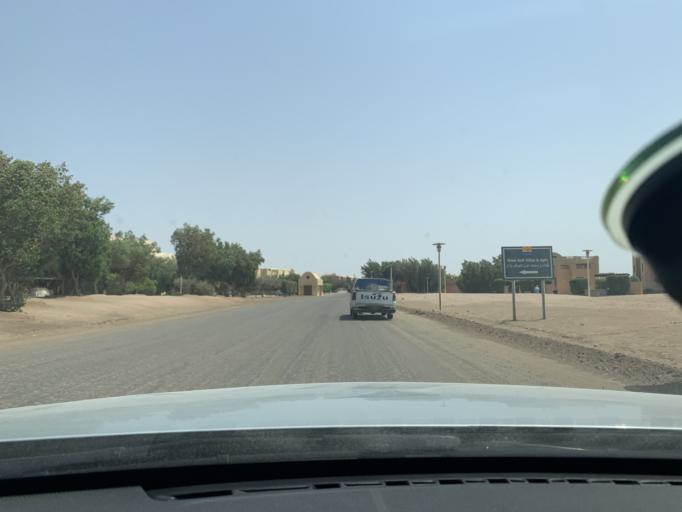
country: EG
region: Red Sea
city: El Gouna
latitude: 27.3883
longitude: 33.6692
